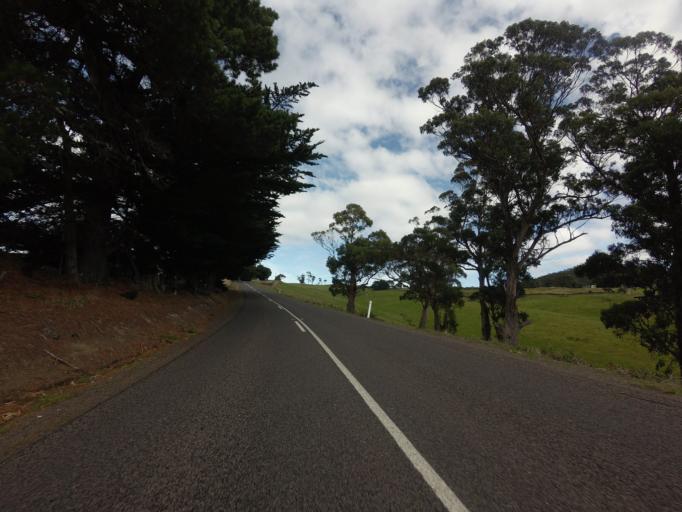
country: AU
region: Tasmania
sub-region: Clarence
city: Sandford
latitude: -43.0637
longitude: 147.7496
